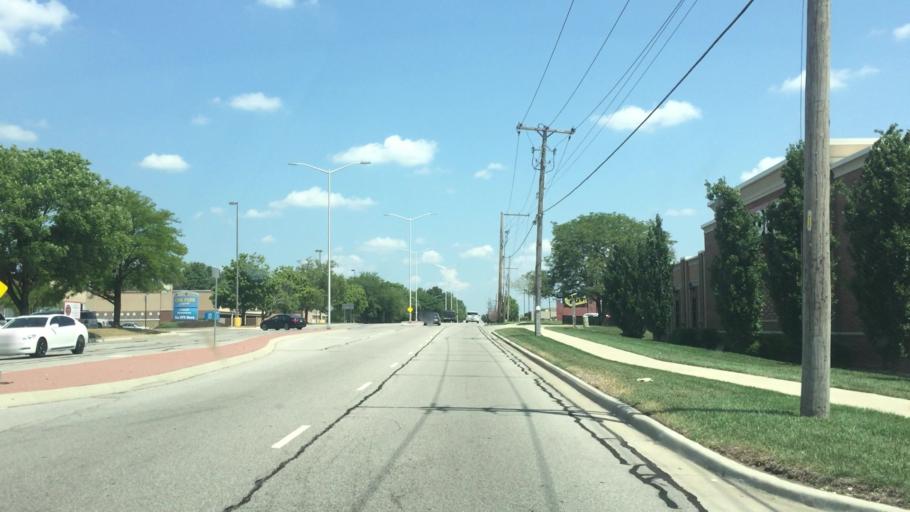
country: US
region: Kansas
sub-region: Johnson County
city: Lenexa
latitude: 38.9575
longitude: -94.7235
